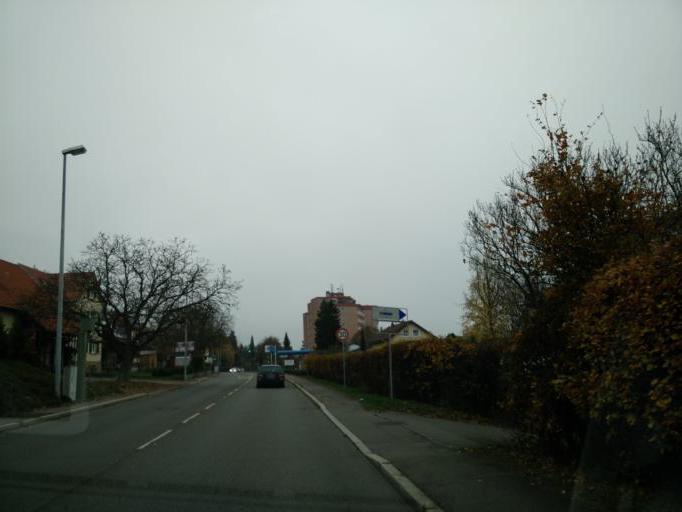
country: DE
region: Baden-Wuerttemberg
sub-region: Tuebingen Region
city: Tuebingen
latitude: 48.5249
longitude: 8.9855
